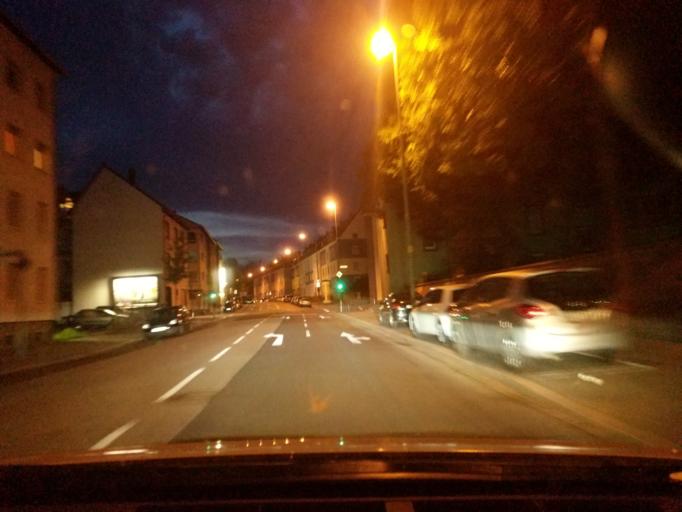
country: DE
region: Rheinland-Pfalz
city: Kaiserslautern
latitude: 49.4451
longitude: 7.7844
